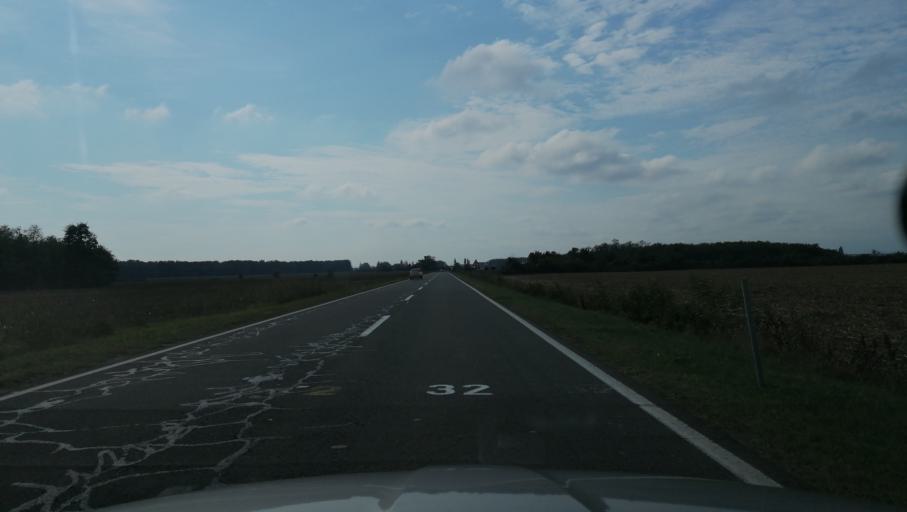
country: RS
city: Bosut
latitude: 44.9569
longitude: 19.3780
